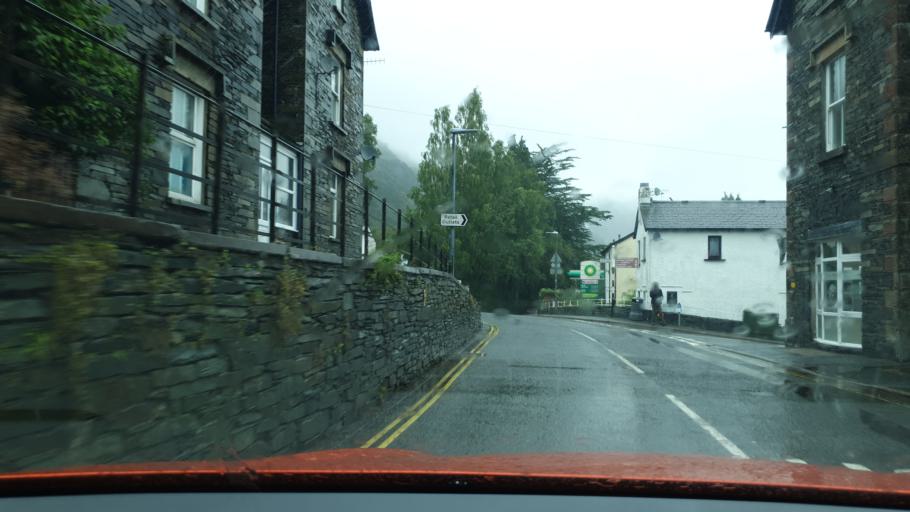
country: GB
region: England
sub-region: Cumbria
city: Ambleside
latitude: 54.3678
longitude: -3.0767
